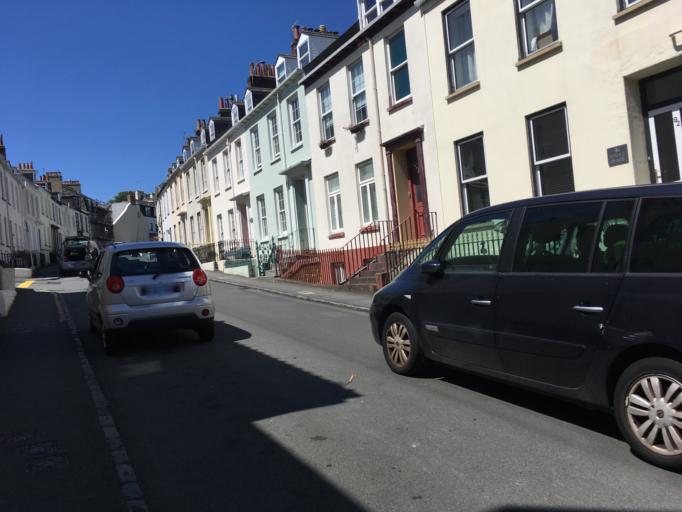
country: GG
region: St Peter Port
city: Saint Peter Port
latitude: 49.4545
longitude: -2.5461
